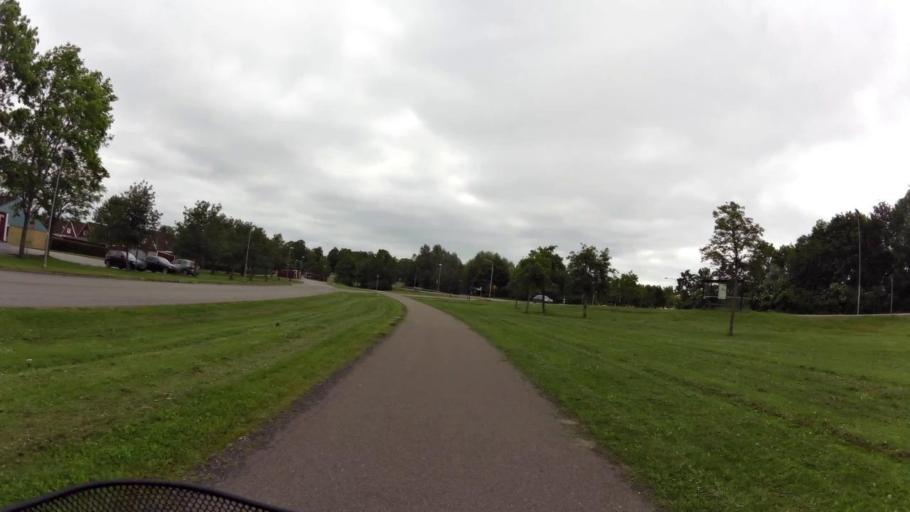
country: SE
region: OEstergoetland
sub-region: Linkopings Kommun
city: Linkoping
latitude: 58.3741
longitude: 15.6580
